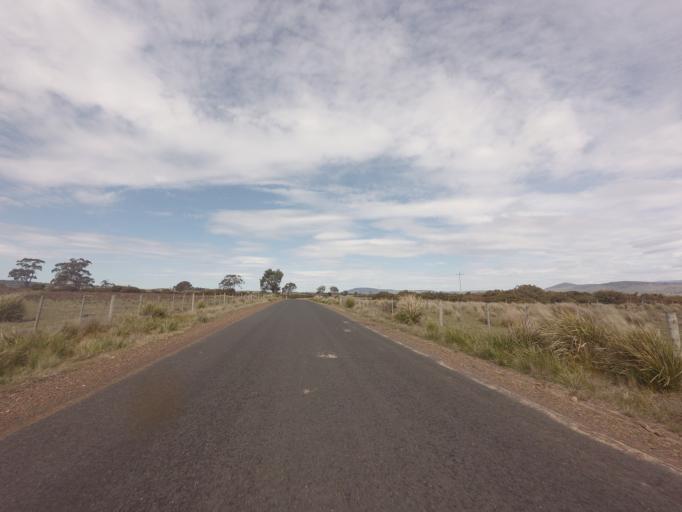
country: AU
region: Tasmania
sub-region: Northern Midlands
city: Evandale
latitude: -41.8333
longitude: 147.3281
